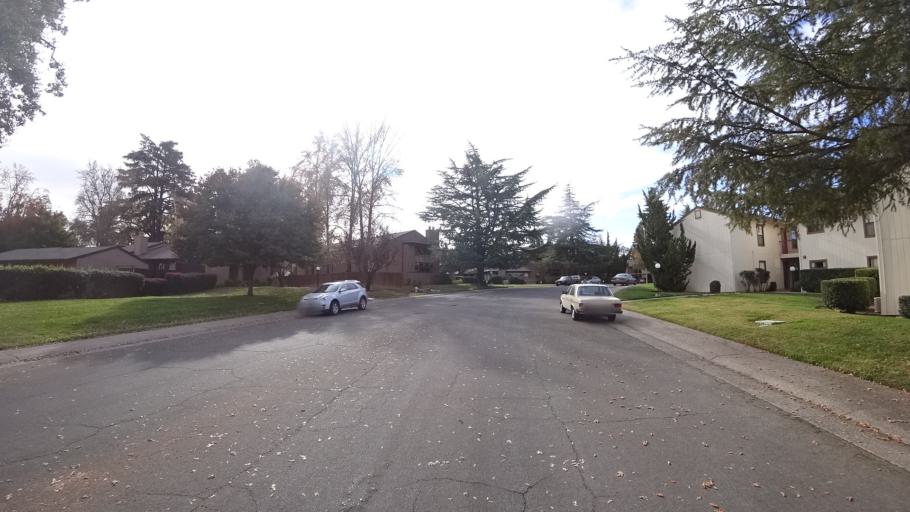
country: US
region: California
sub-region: Sacramento County
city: Fair Oaks
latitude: 38.6685
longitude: -121.2694
